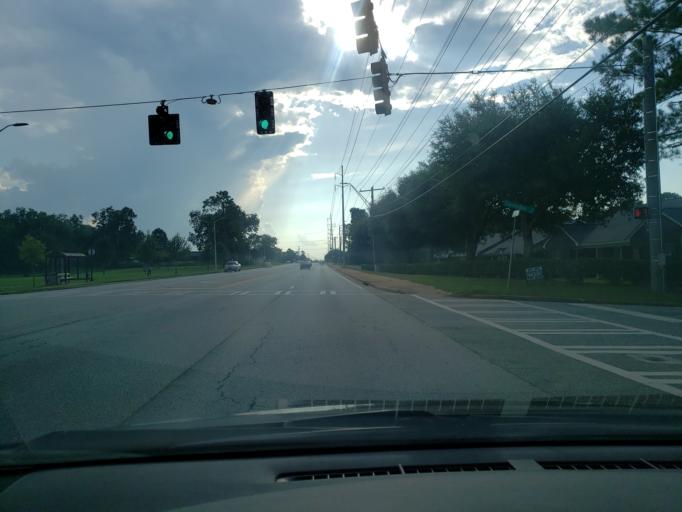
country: US
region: Georgia
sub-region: Dougherty County
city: Albany
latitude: 31.5859
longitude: -84.2140
